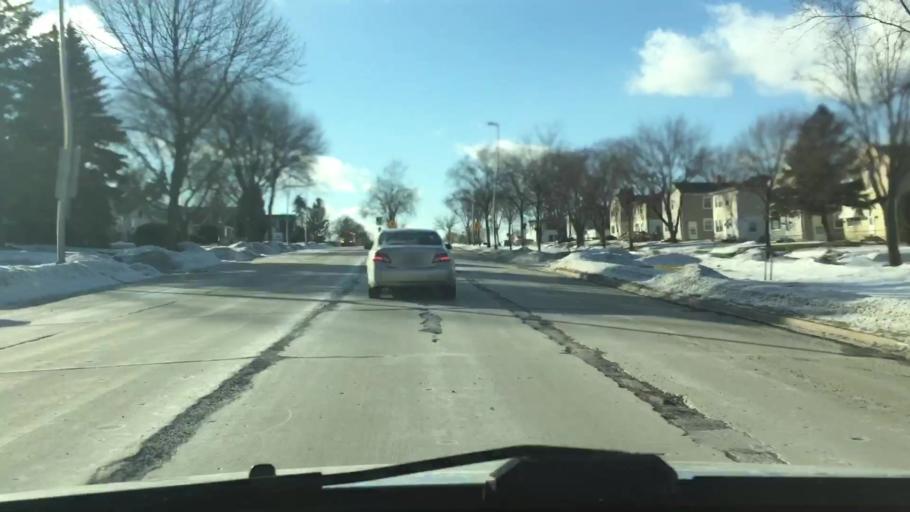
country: US
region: Wisconsin
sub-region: Milwaukee County
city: West Milwaukee
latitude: 42.9739
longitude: -87.9721
